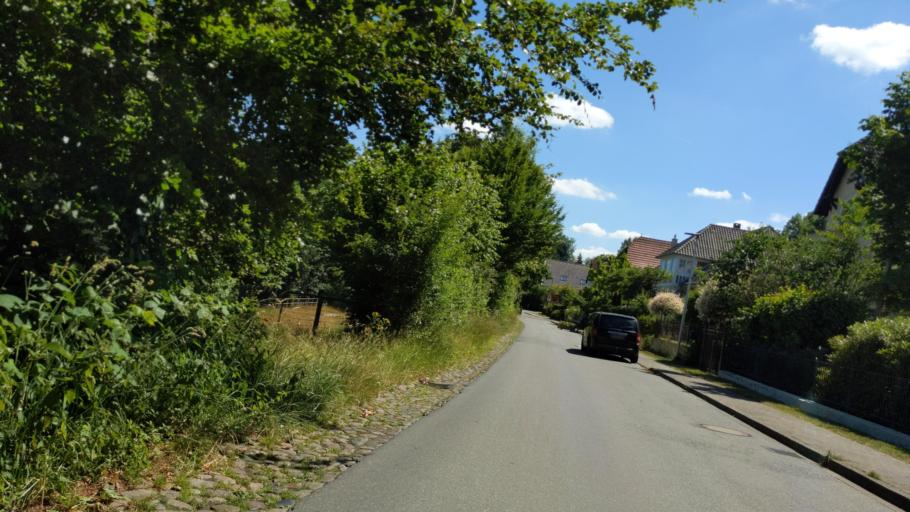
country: DE
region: Schleswig-Holstein
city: Romnitz
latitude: 53.7039
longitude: 10.7502
